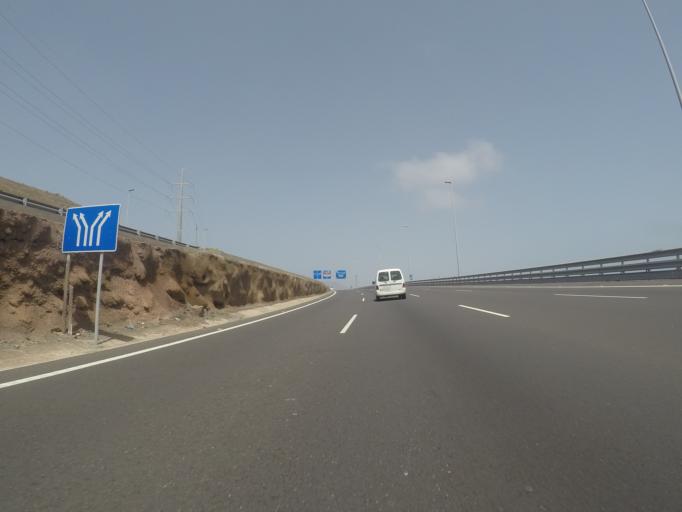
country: ES
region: Canary Islands
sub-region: Provincia de Santa Cruz de Tenerife
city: Santa Cruz de Tenerife
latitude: 28.4388
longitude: -16.2795
